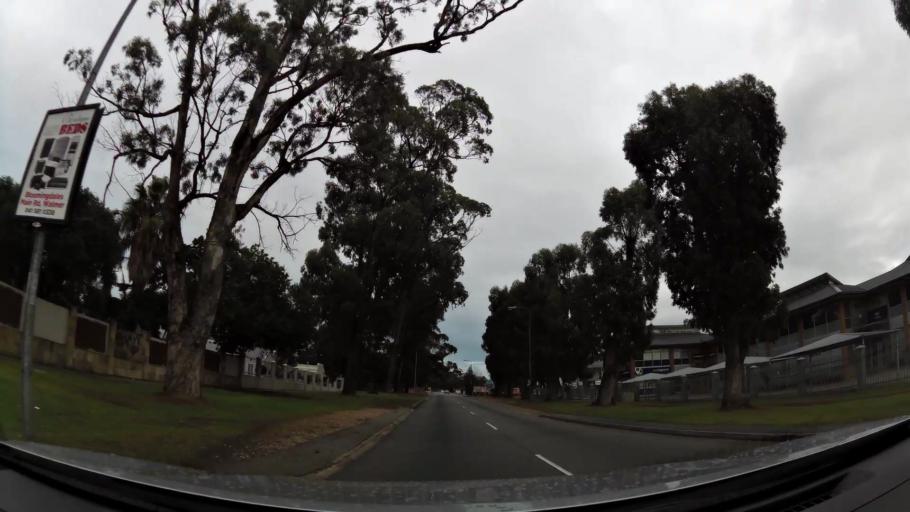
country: ZA
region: Eastern Cape
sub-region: Nelson Mandela Bay Metropolitan Municipality
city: Port Elizabeth
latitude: -33.9794
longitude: 25.5826
